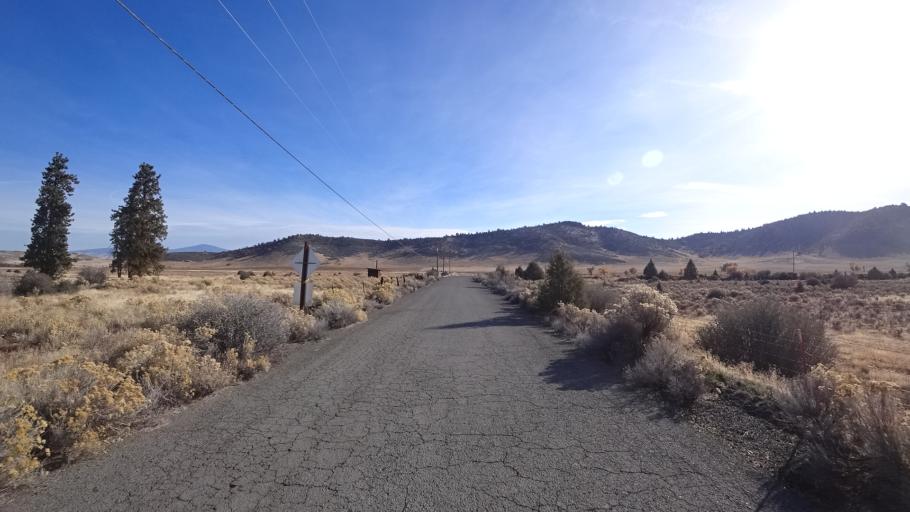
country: US
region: California
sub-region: Siskiyou County
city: Montague
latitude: 41.6368
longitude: -122.5698
